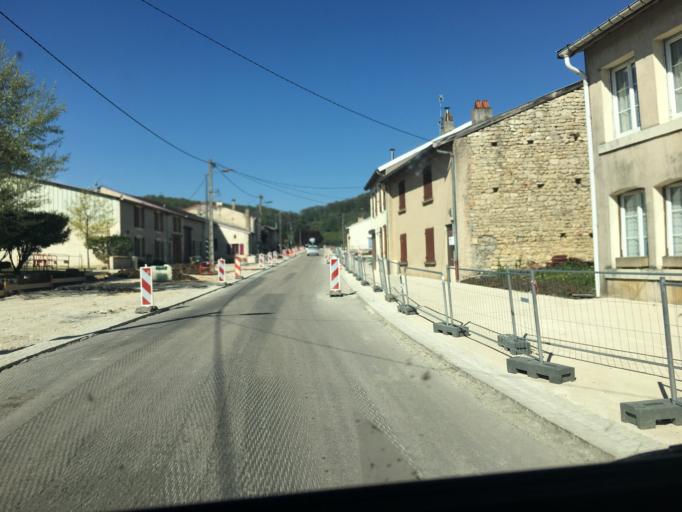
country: FR
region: Lorraine
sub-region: Departement de la Meuse
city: Vigneulles-les-Hattonchatel
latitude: 48.9315
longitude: 5.6943
